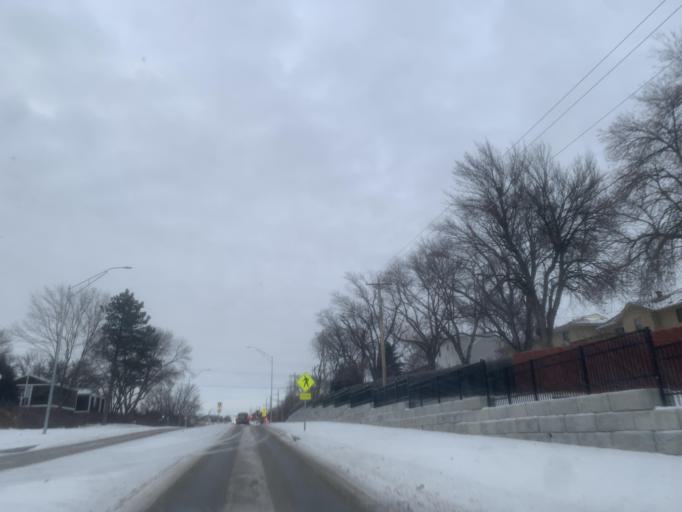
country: US
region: Nebraska
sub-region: Douglas County
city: Ralston
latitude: 41.2741
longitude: -96.0813
